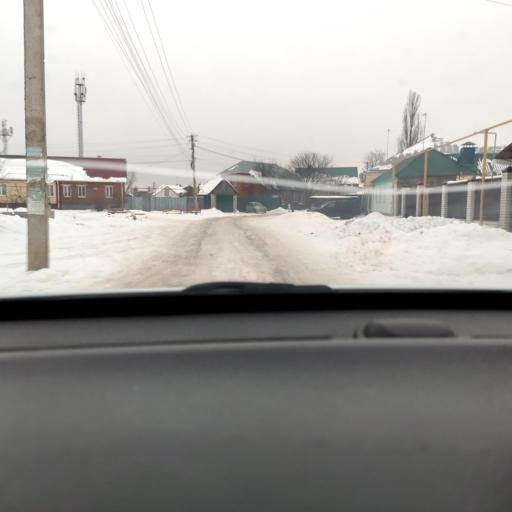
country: RU
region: Voronezj
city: Somovo
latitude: 51.7487
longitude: 39.3400
